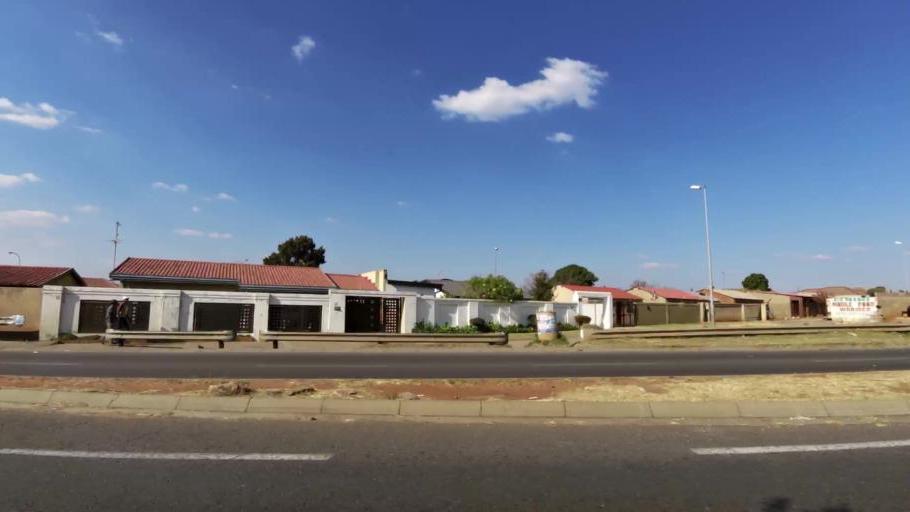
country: ZA
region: Gauteng
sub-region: City of Johannesburg Metropolitan Municipality
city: Soweto
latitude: -26.2268
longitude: 27.8729
